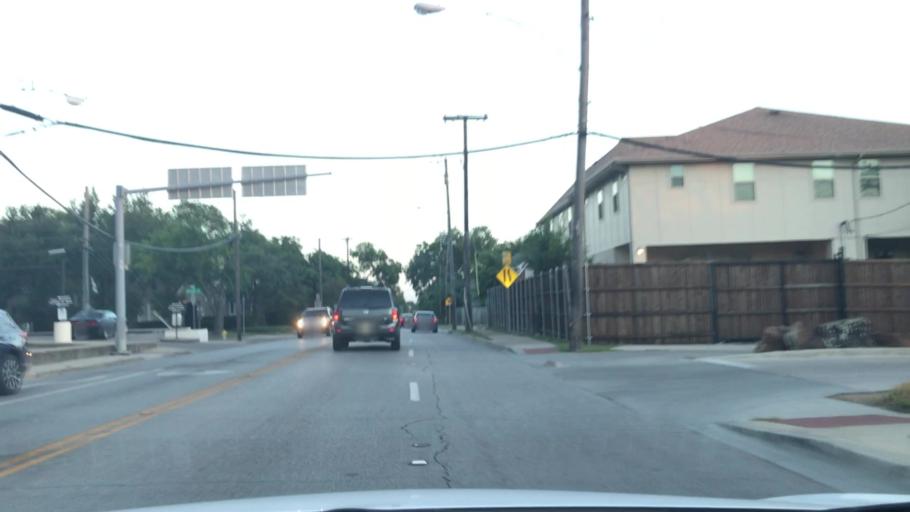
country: US
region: Texas
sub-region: Dallas County
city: Highland Park
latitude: 32.8363
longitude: -96.7701
